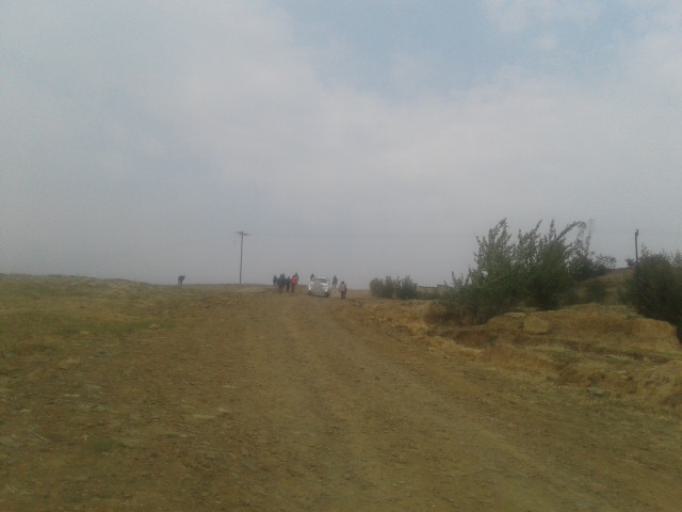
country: LS
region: Berea
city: Teyateyaneng
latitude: -29.0852
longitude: 27.9051
